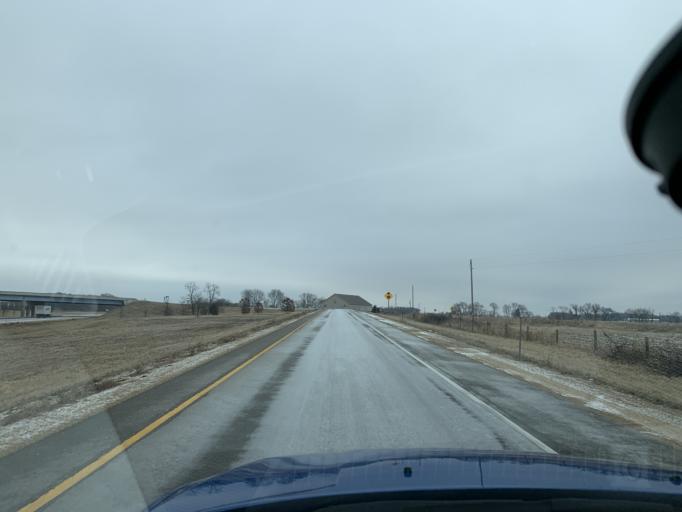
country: US
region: Wisconsin
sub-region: Dane County
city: Marshall
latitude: 43.2662
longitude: -89.1083
